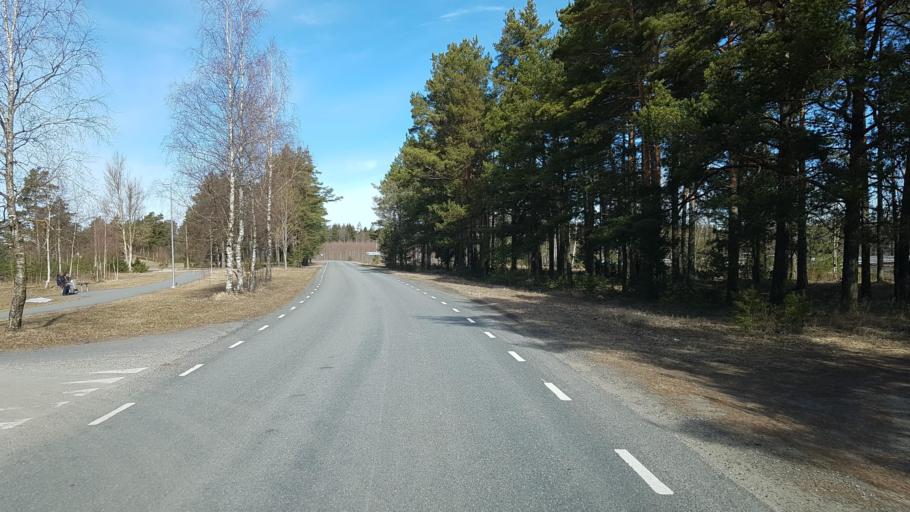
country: EE
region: Harju
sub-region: Nissi vald
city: Riisipere
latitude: 59.2470
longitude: 24.2419
